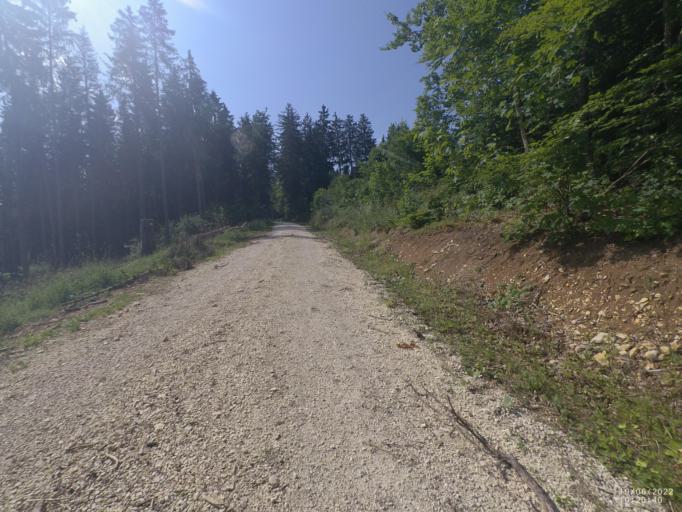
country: DE
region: Baden-Wuerttemberg
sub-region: Regierungsbezirk Stuttgart
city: Gerstetten
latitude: 48.6056
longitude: 9.9989
